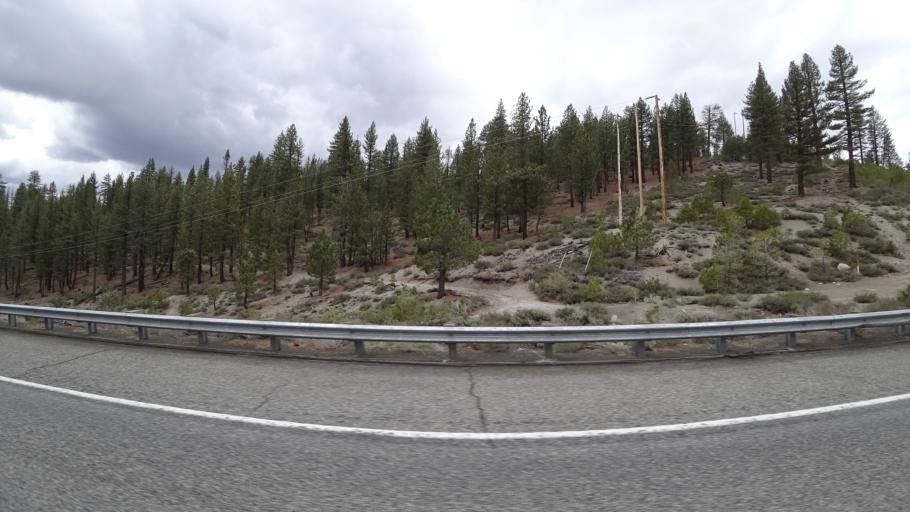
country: US
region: California
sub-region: Mono County
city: Mammoth Lakes
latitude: 37.7609
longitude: -118.9938
